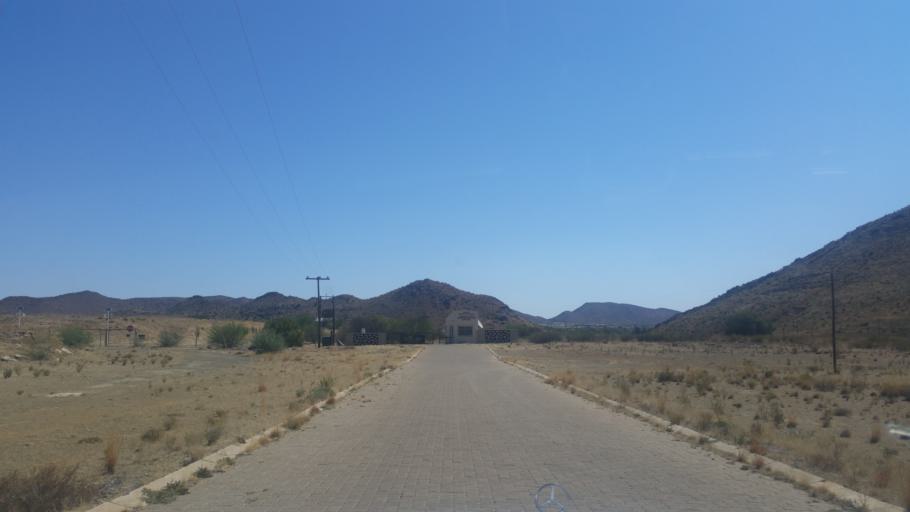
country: ZA
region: Northern Cape
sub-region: Pixley ka Seme District Municipality
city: Colesberg
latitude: -30.6242
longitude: 25.4766
